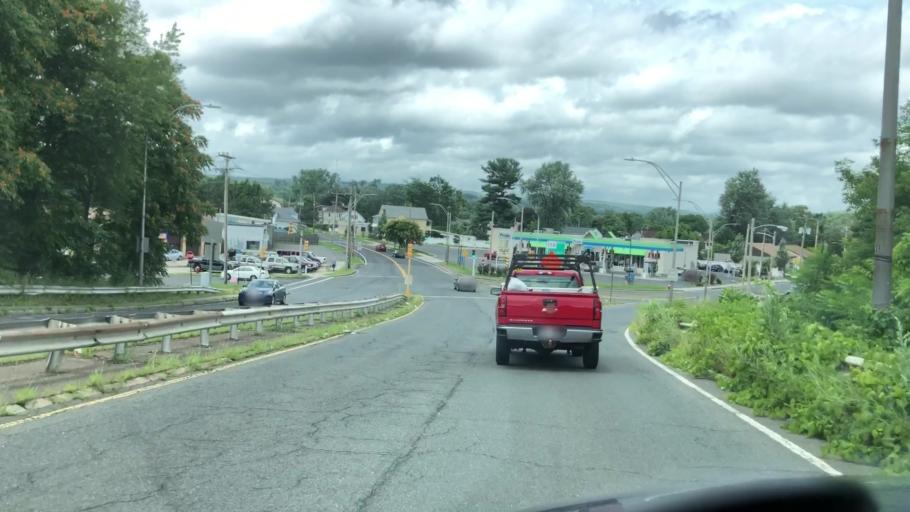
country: US
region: Massachusetts
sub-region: Hampden County
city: Chicopee
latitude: 42.1598
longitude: -72.6132
